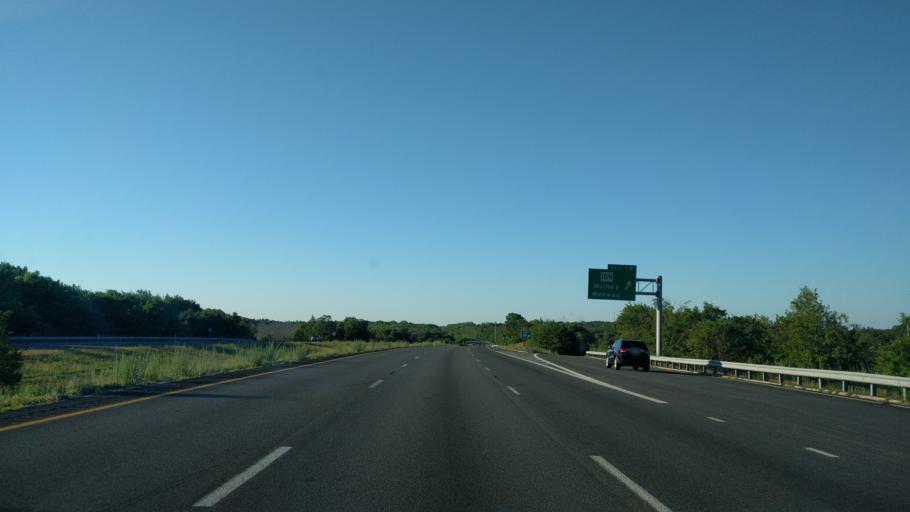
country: US
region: Massachusetts
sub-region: Worcester County
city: Milford
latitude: 42.1514
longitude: -71.4862
